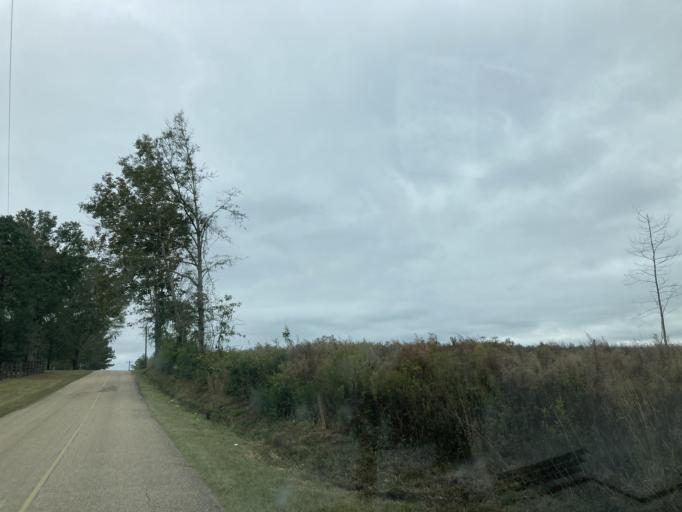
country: US
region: Mississippi
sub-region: Lamar County
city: West Hattiesburg
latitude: 31.2651
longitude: -89.5058
